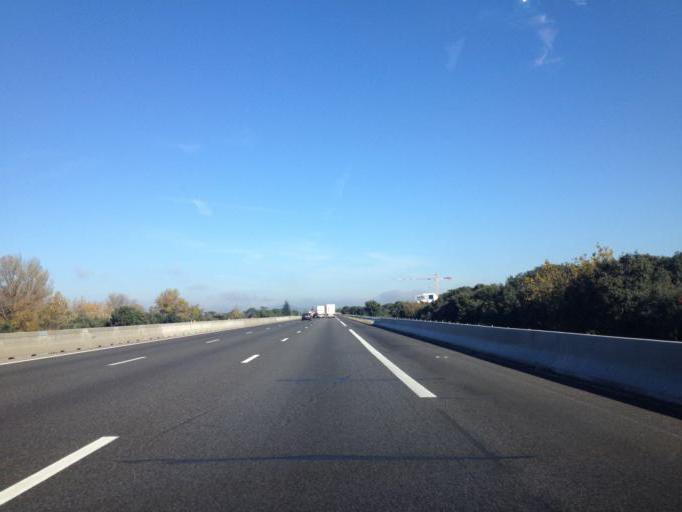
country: FR
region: Rhone-Alpes
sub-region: Departement de la Drome
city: Saint-Paul-Trois-Chateaux
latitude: 44.3443
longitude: 4.7379
